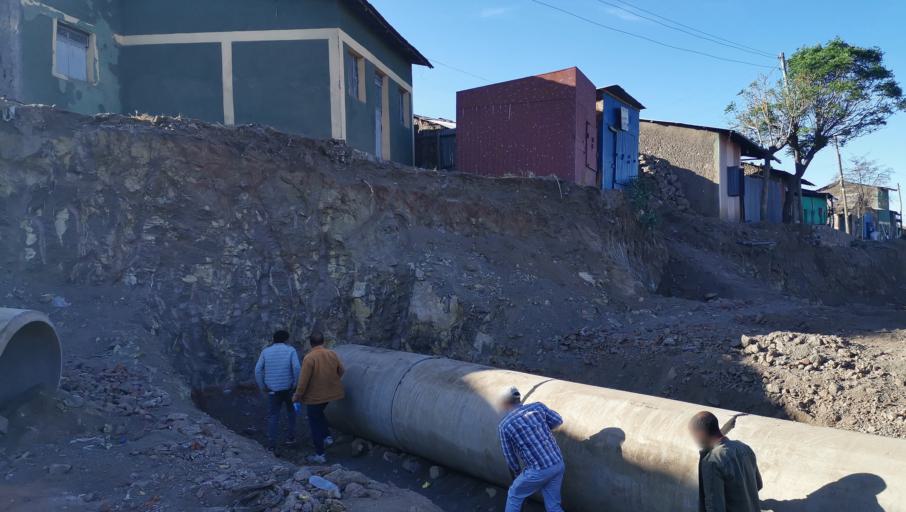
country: ET
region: Tigray
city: Korem
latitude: 12.6292
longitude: 39.0352
